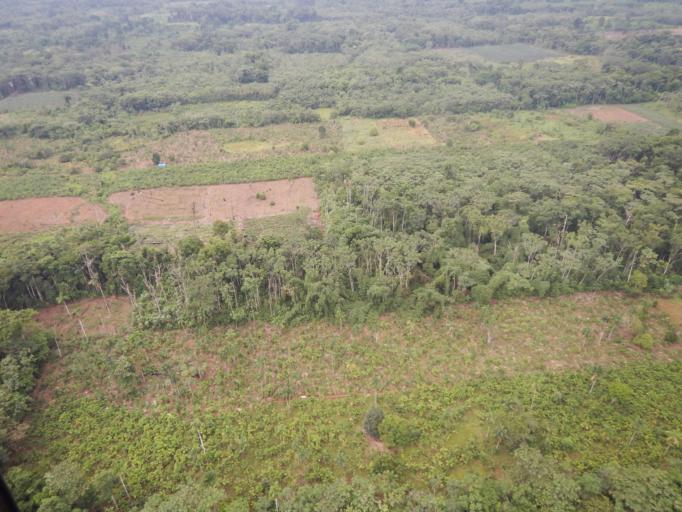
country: BO
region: Cochabamba
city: Chimore
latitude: -17.2432
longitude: -64.6782
